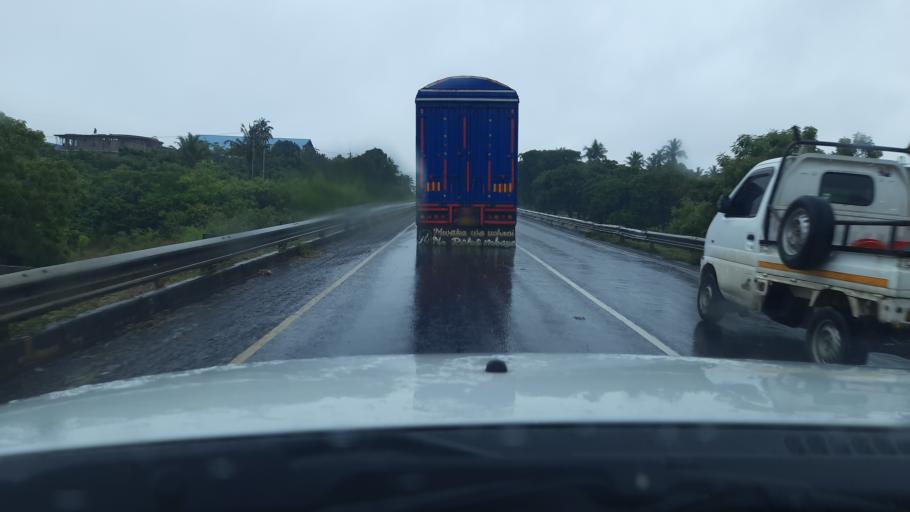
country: TZ
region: Pwani
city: Bagamoyo
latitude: -6.5864
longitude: 39.0506
